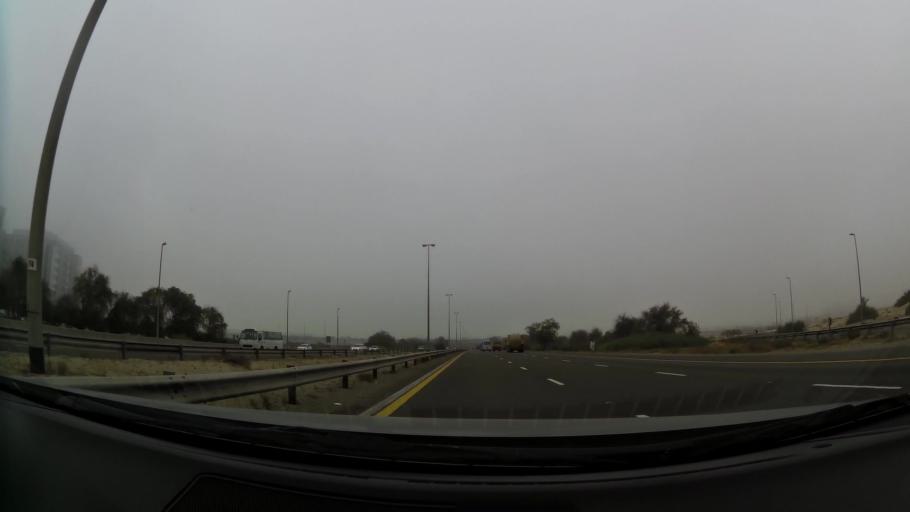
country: AE
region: Dubai
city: Dubai
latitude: 25.1072
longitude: 55.3755
